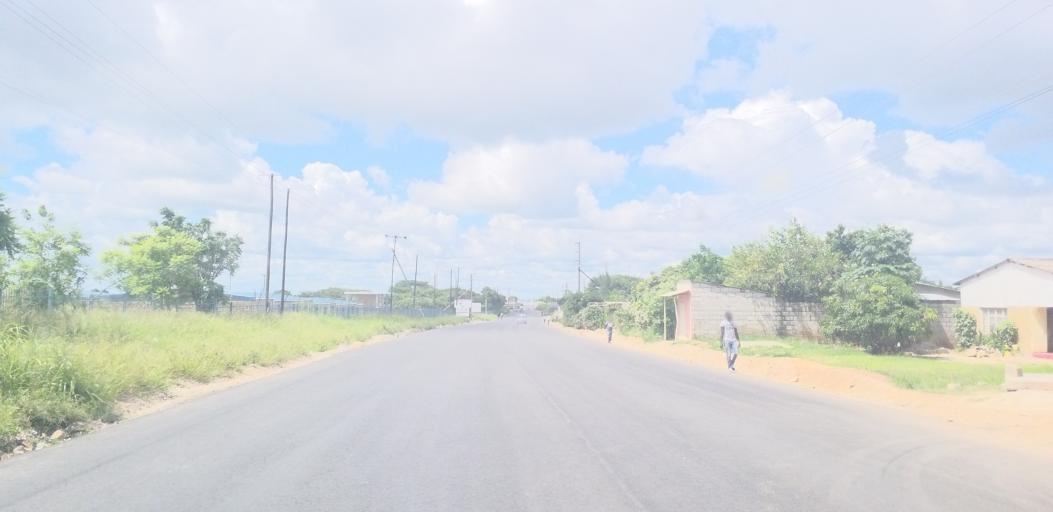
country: ZM
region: Lusaka
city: Lusaka
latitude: -15.3584
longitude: 28.3227
